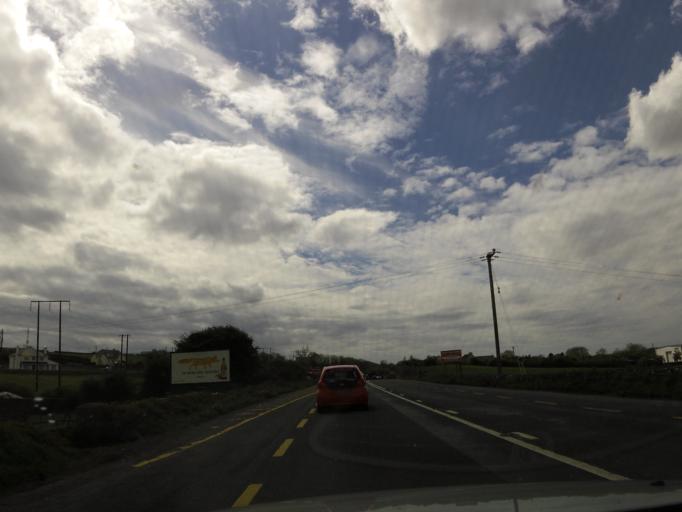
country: IE
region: Connaught
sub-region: County Galway
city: Claregalway
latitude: 53.3098
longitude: -8.9905
